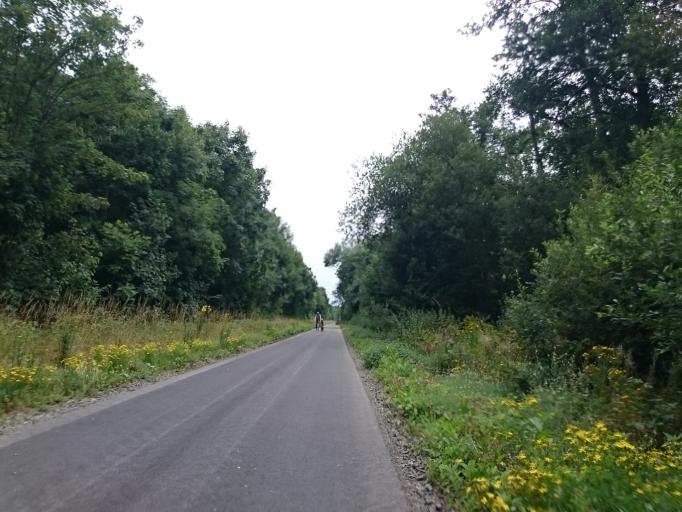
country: FR
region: Lower Normandy
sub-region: Departement du Calvados
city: Thury-Harcourt
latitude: 49.0262
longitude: -0.4644
